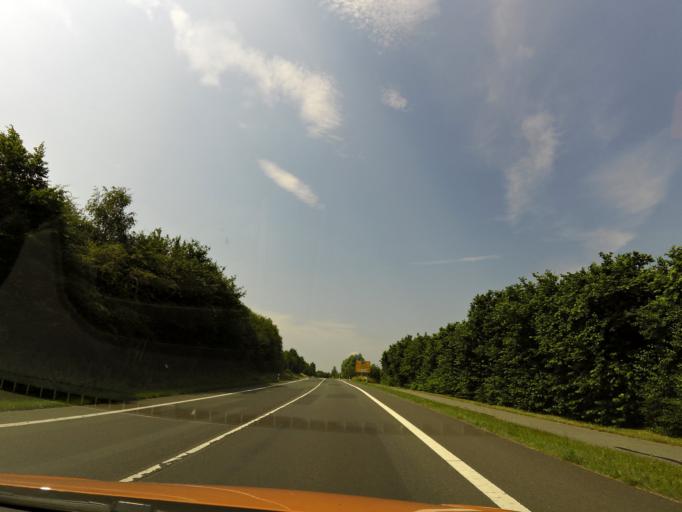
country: DE
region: Brandenburg
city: Gerdshagen
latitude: 53.2104
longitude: 12.2110
